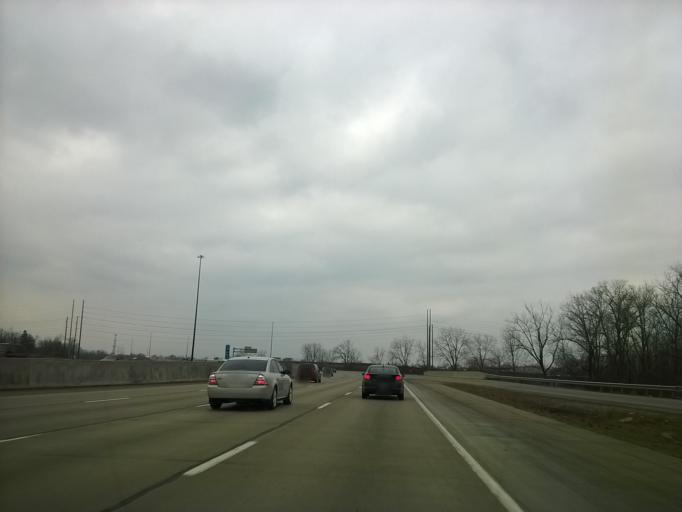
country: US
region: Indiana
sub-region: Marion County
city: Warren Park
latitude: 39.8024
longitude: -86.0865
